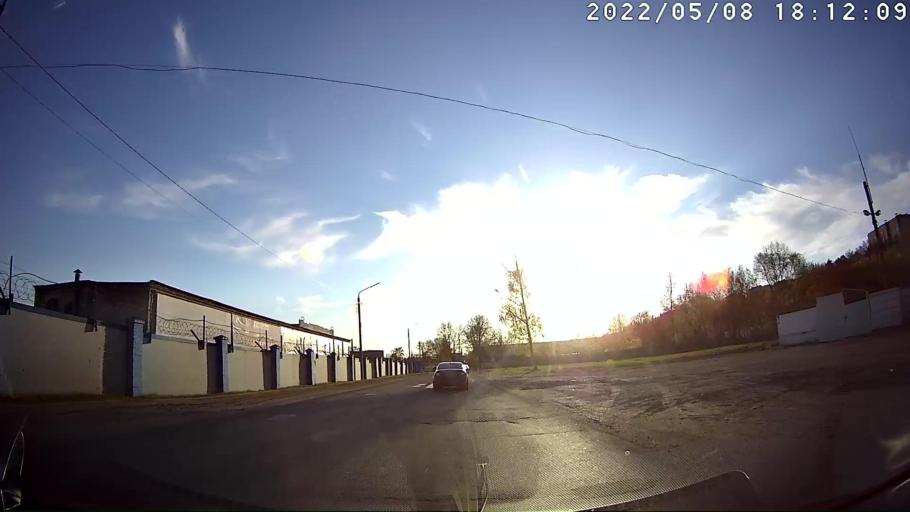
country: RU
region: Tatarstan
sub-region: Zelenodol'skiy Rayon
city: Zelenodolsk
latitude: 55.8408
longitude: 48.5049
